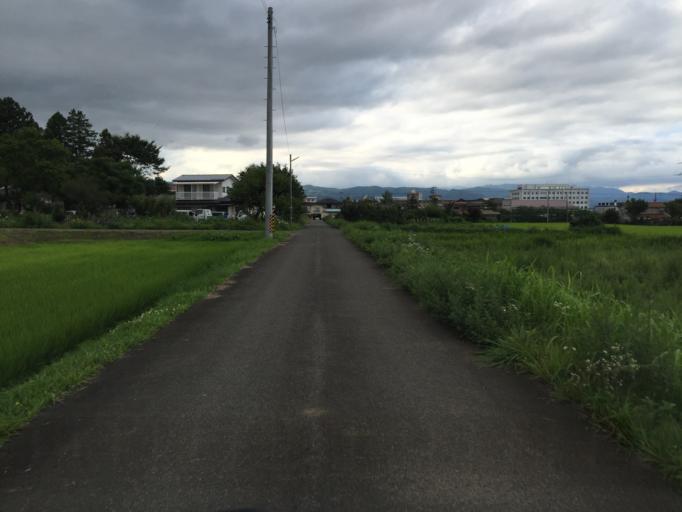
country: JP
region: Fukushima
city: Fukushima-shi
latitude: 37.7219
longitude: 140.3888
